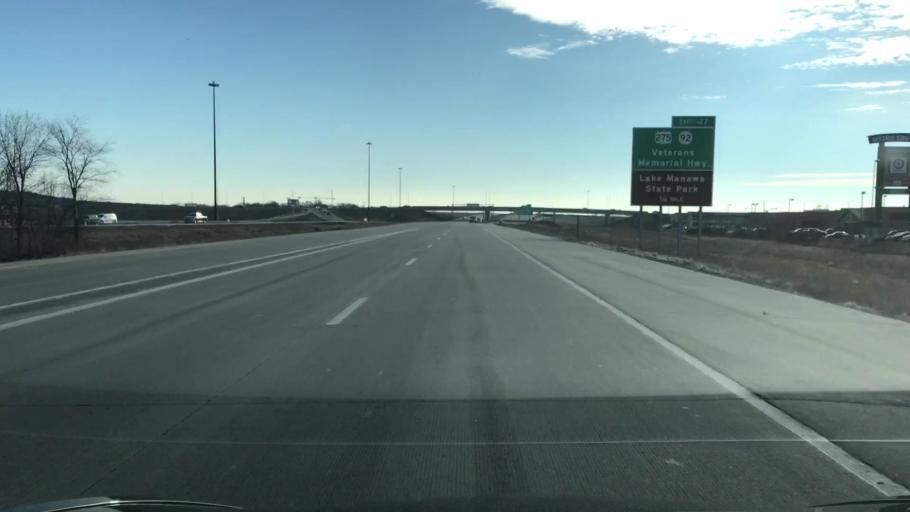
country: US
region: Iowa
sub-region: Pottawattamie County
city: Council Bluffs
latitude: 41.2245
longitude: -95.8368
